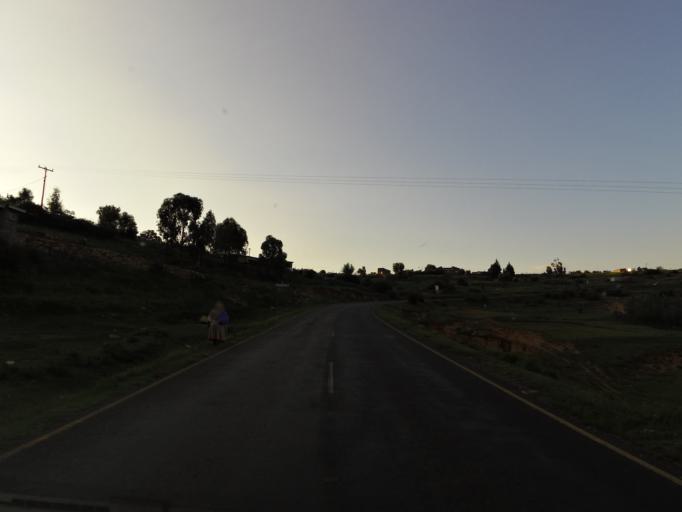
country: LS
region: Leribe
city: Leribe
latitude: -28.8895
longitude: 28.1029
